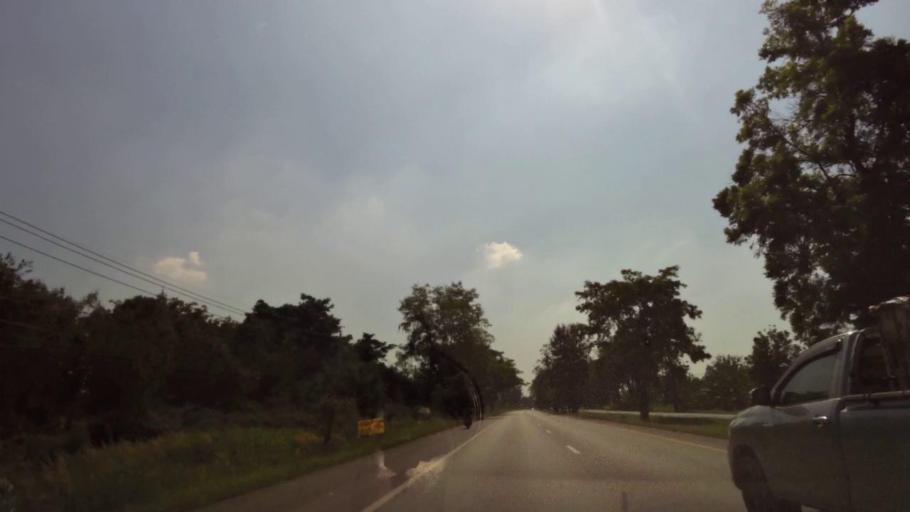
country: TH
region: Phichit
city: Bueng Na Rang
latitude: 16.1826
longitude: 100.1286
